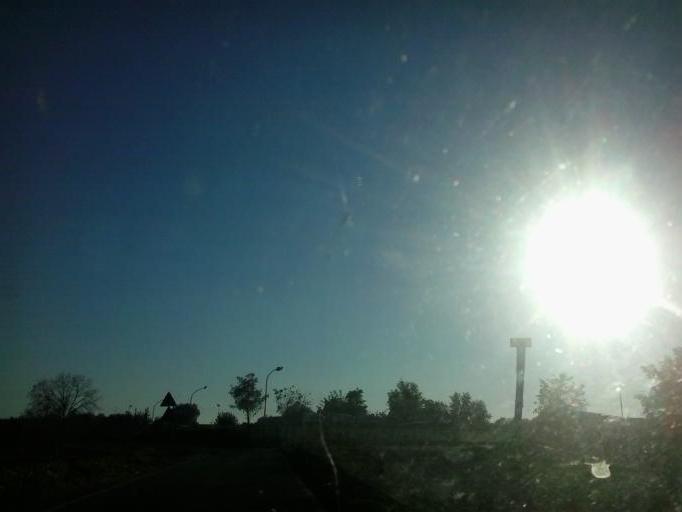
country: IT
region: Lombardy
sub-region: Provincia di Brescia
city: Azzano Mella
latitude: 45.4256
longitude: 10.1286
